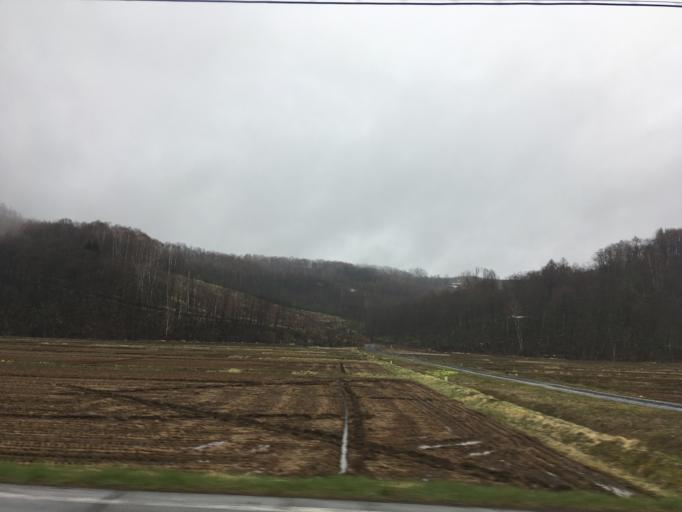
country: JP
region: Hokkaido
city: Nayoro
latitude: 44.0899
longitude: 142.4236
